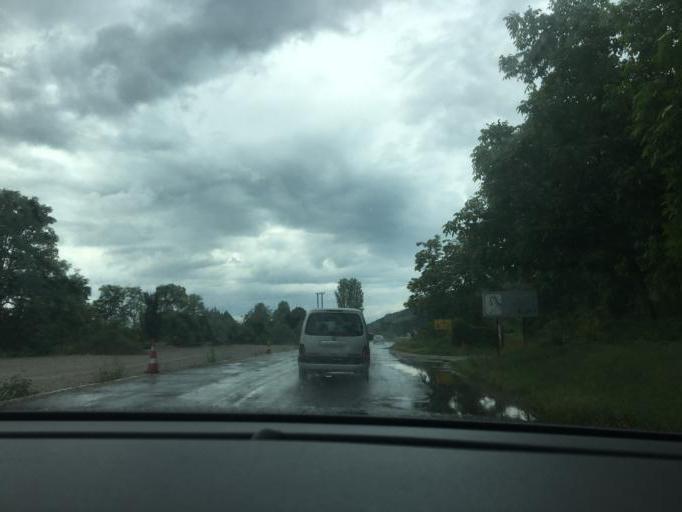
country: MK
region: Ohrid
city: Ohrid
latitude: 41.1428
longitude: 20.7606
